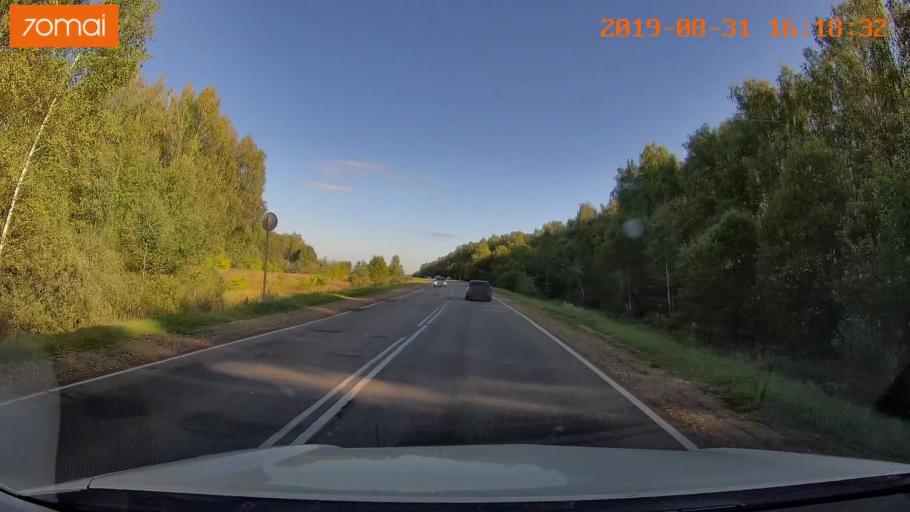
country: RU
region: Kaluga
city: Nikola-Lenivets
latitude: 54.5359
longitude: 35.5563
